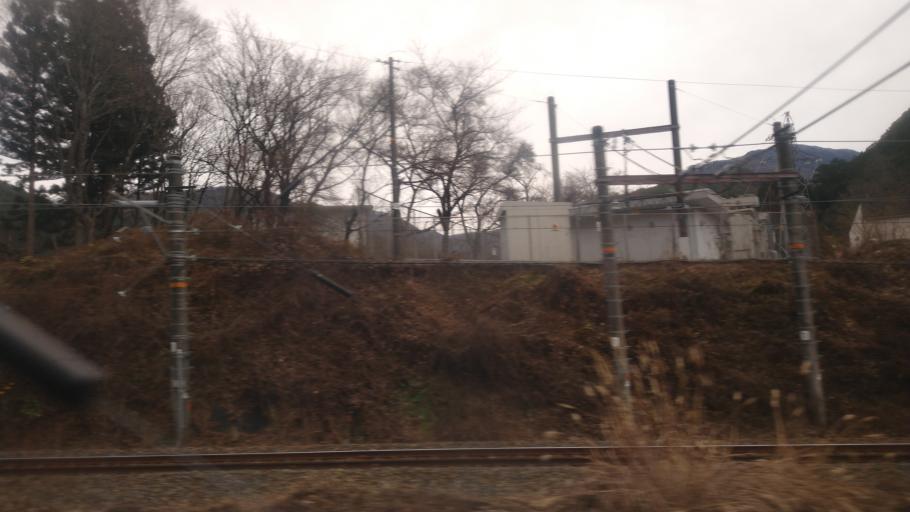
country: JP
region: Nagano
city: Ina
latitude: 35.8989
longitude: 137.7686
